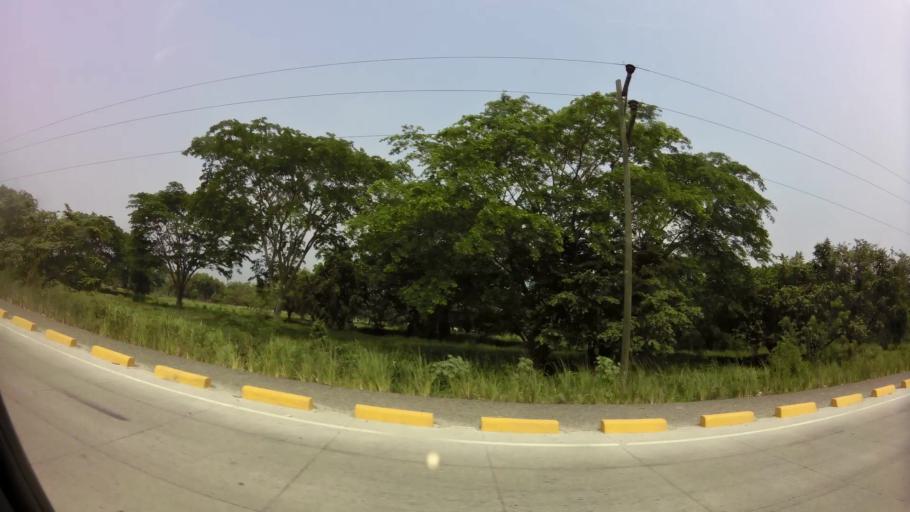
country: HN
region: Cortes
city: San Pedro Sula
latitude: 15.5457
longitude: -87.9983
